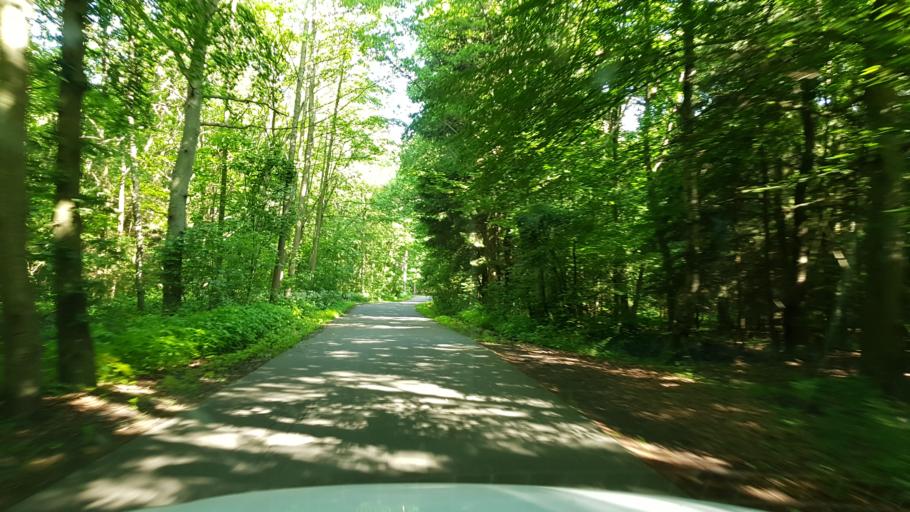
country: PL
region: West Pomeranian Voivodeship
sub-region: Powiat kolobrzeski
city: Ustronie Morskie
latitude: 54.2154
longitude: 15.7754
